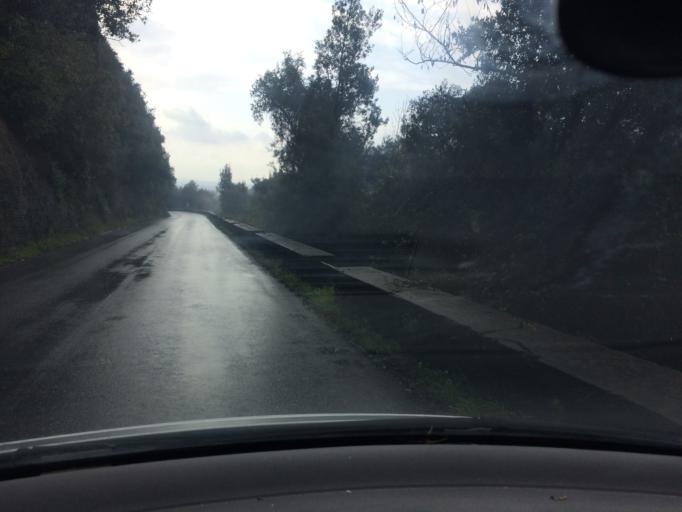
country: IT
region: Tuscany
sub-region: Provincia di Massa-Carrara
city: Massa
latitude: 44.0628
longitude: 10.1174
